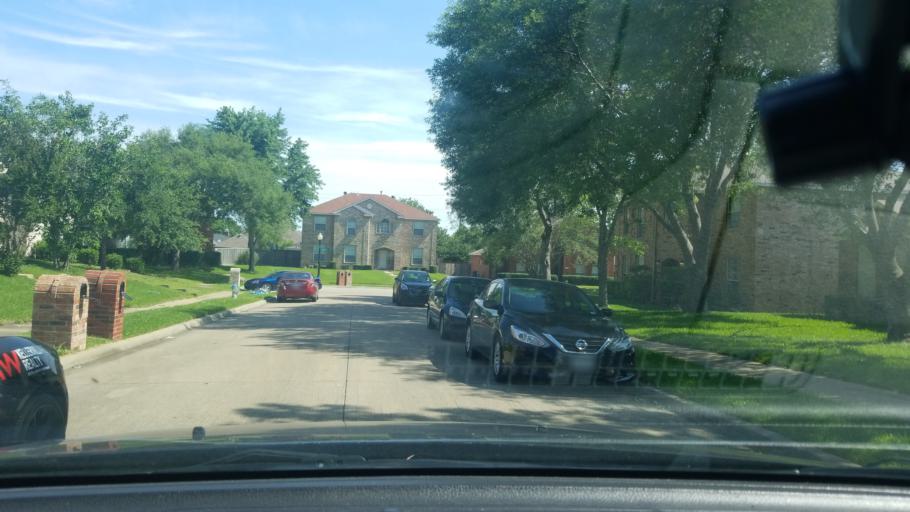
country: US
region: Texas
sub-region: Dallas County
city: Mesquite
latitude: 32.7737
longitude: -96.5908
